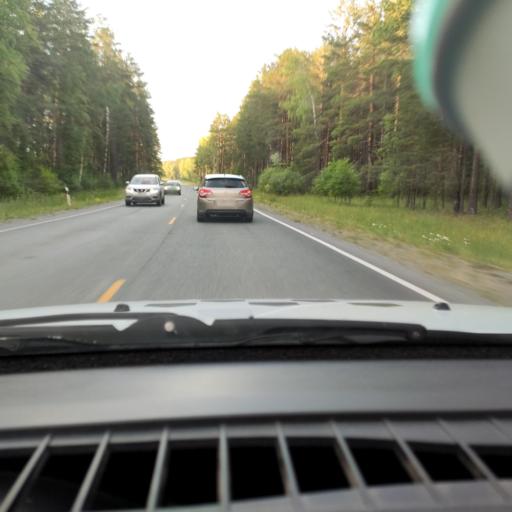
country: RU
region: Chelyabinsk
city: Turgoyak
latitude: 55.2814
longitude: 60.1974
